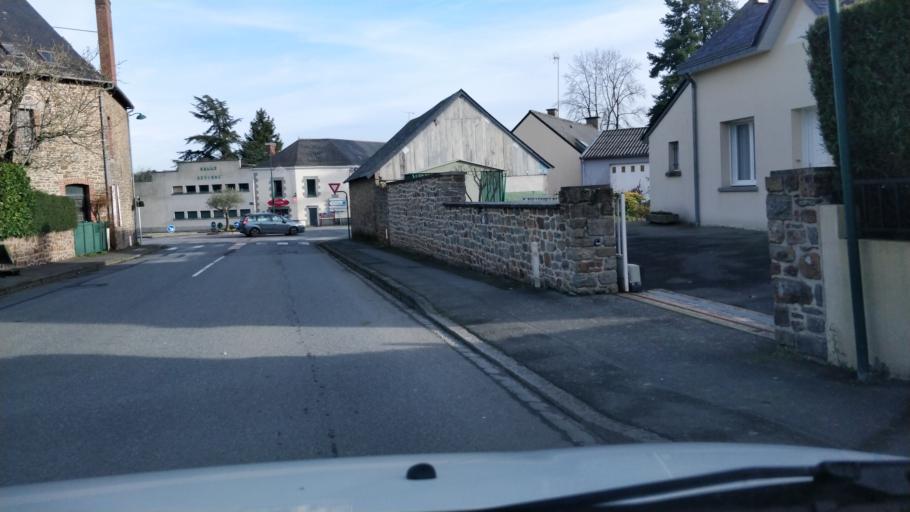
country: FR
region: Brittany
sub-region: Departement d'Ille-et-Vilaine
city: Argentre-du-Plessis
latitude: 48.0564
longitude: -1.1557
